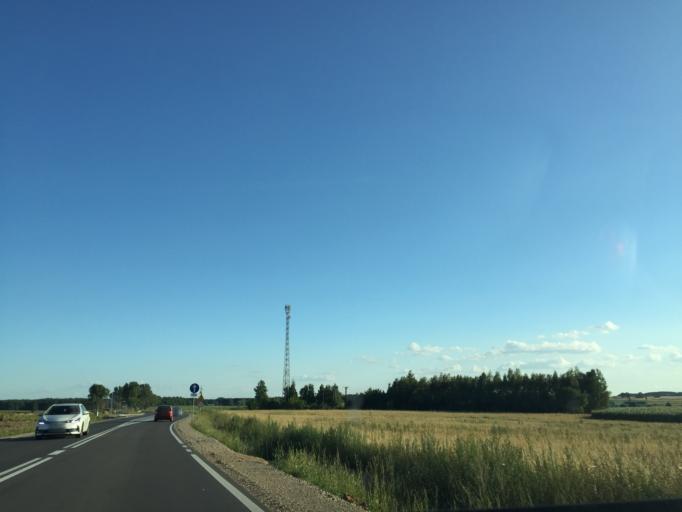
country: PL
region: Podlasie
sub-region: Powiat kolnenski
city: Stawiski
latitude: 53.3247
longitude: 22.1528
